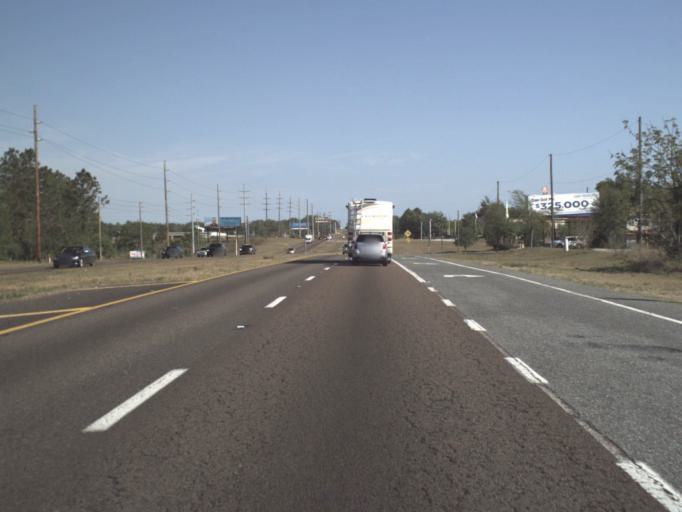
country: US
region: Florida
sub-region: Lake County
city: Minneola
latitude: 28.5924
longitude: -81.7524
